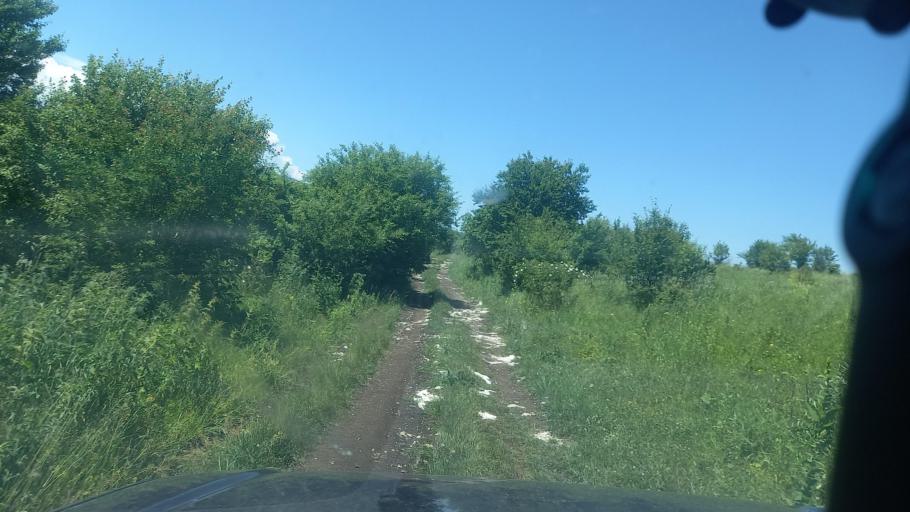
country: RU
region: Karachayevo-Cherkesiya
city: Pregradnaya
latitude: 44.1052
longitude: 41.1315
